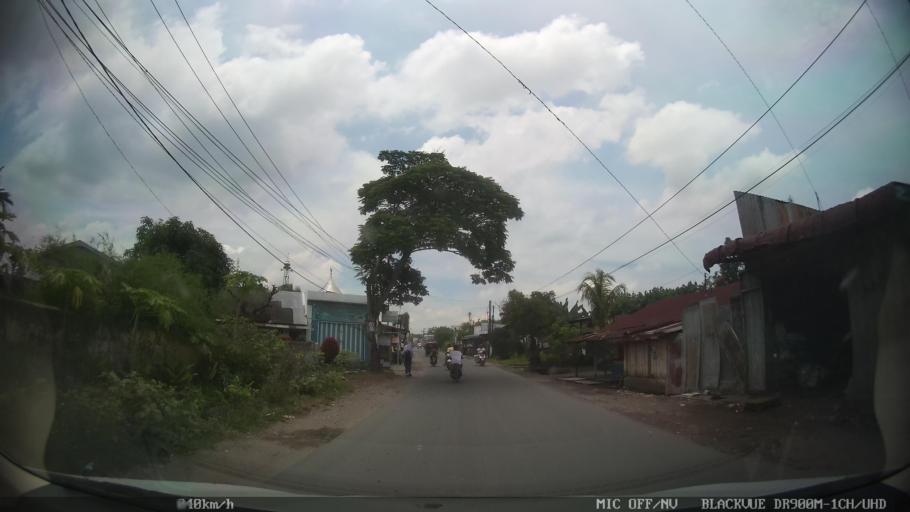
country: ID
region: North Sumatra
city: Labuhan Deli
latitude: 3.6831
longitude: 98.6688
